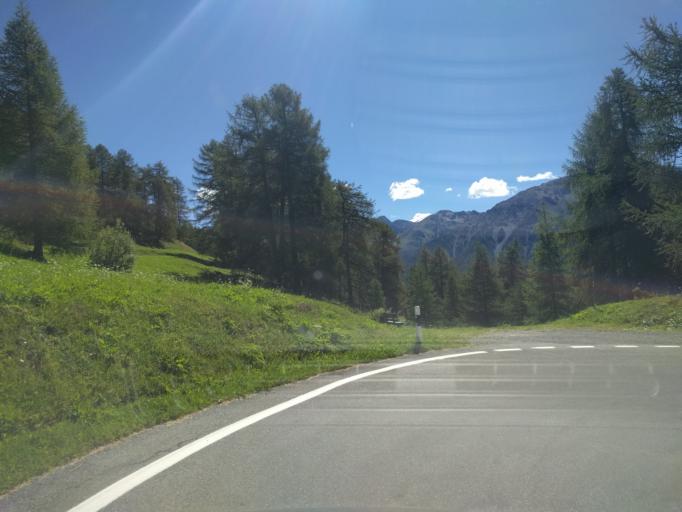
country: IT
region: Trentino-Alto Adige
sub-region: Bolzano
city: Tubre
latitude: 46.6190
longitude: 10.3725
